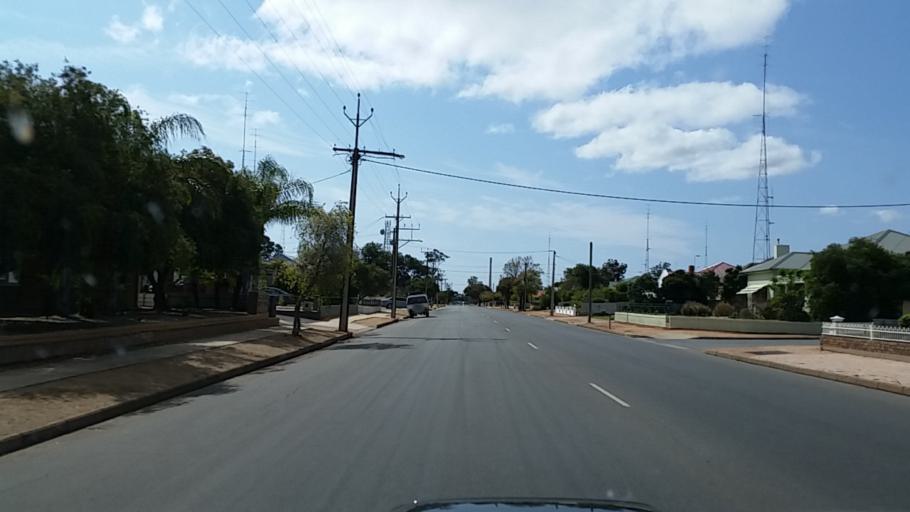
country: AU
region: South Australia
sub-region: Port Pirie City and Dists
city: Port Pirie
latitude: -33.2008
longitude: 138.0102
